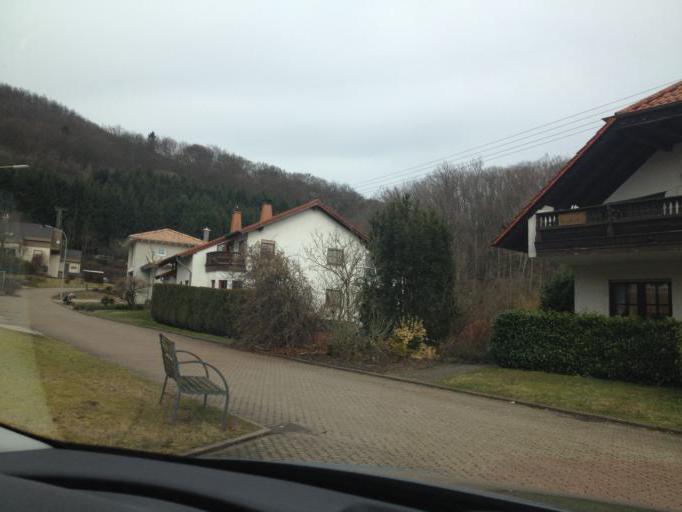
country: DE
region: Saarland
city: Oberthal
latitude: 49.5154
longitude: 7.0684
